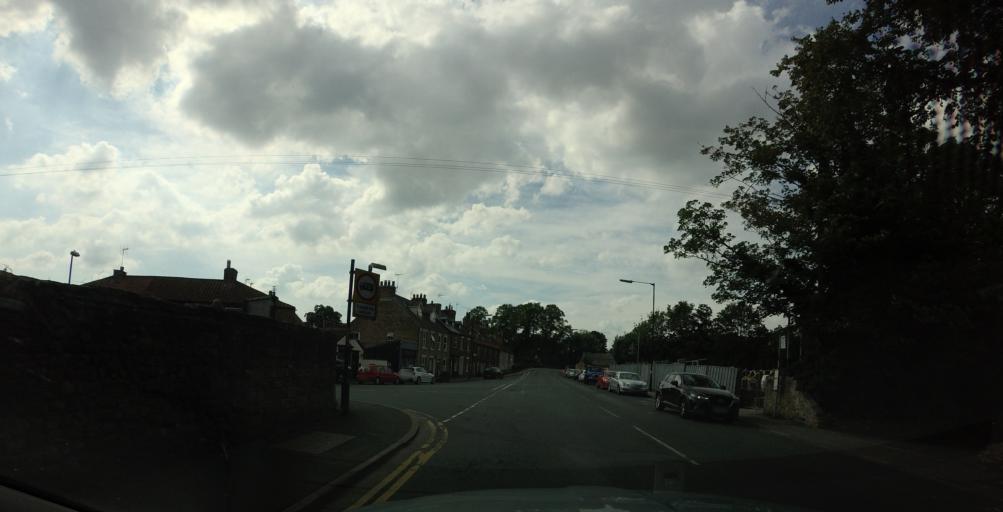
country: GB
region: England
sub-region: North Yorkshire
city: Ripon
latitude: 54.1330
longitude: -1.5191
